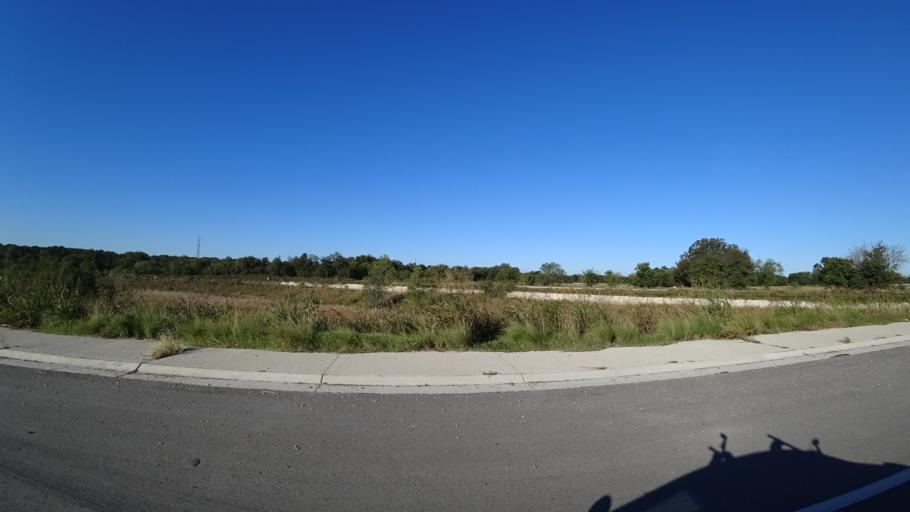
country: US
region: Texas
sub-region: Travis County
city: Hornsby Bend
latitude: 30.2130
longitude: -97.6389
